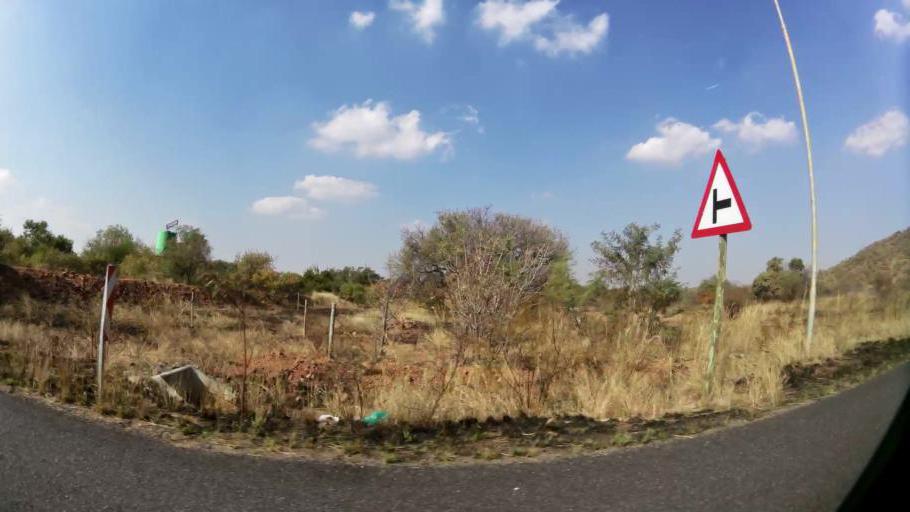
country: ZA
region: North-West
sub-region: Bojanala Platinum District Municipality
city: Rustenburg
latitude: -25.5676
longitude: 27.1413
